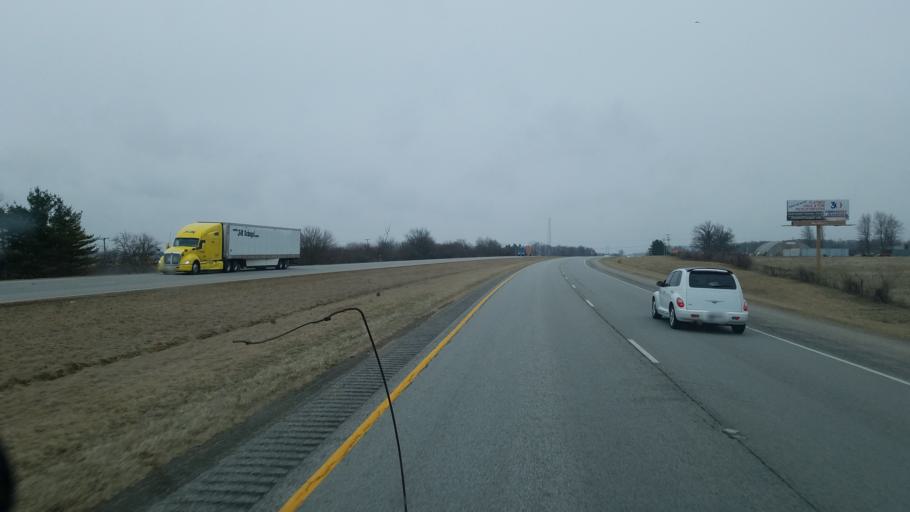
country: US
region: Indiana
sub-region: Miami County
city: Peru
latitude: 40.8842
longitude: -86.1449
